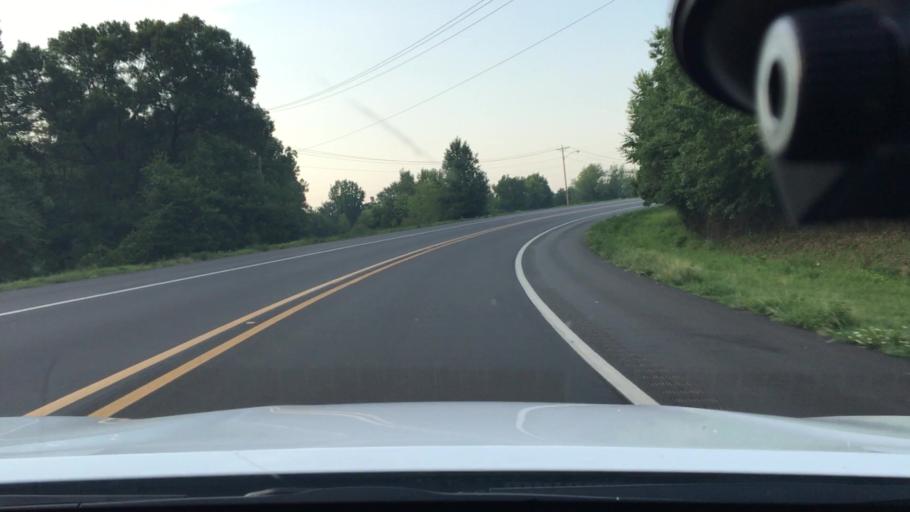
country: US
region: Arkansas
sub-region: Johnson County
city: Clarksville
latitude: 35.4517
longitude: -93.5296
